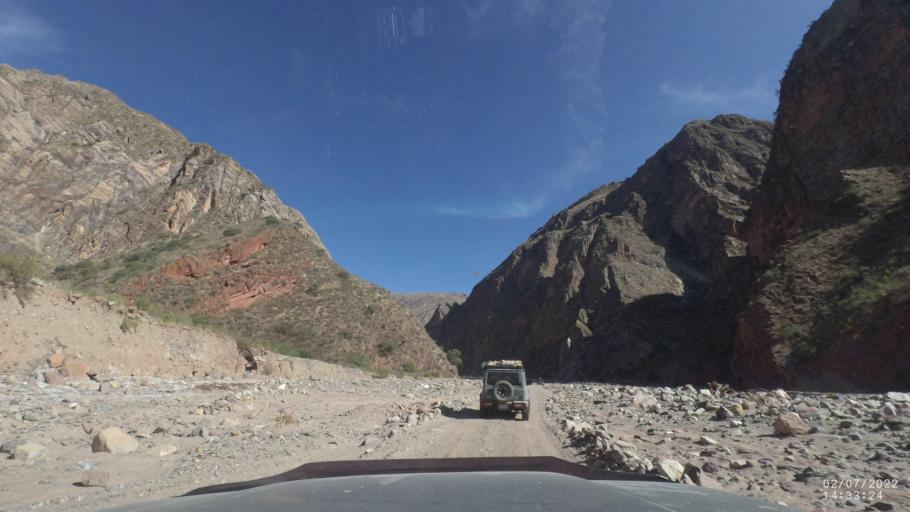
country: BO
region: Cochabamba
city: Irpa Irpa
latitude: -17.8379
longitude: -66.4155
